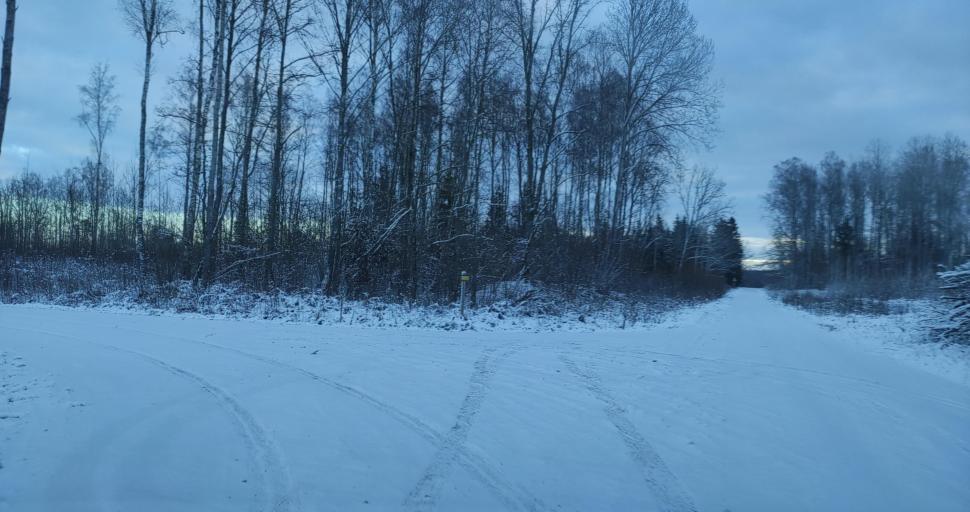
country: LV
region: Vainode
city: Vainode
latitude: 56.5699
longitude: 21.9205
